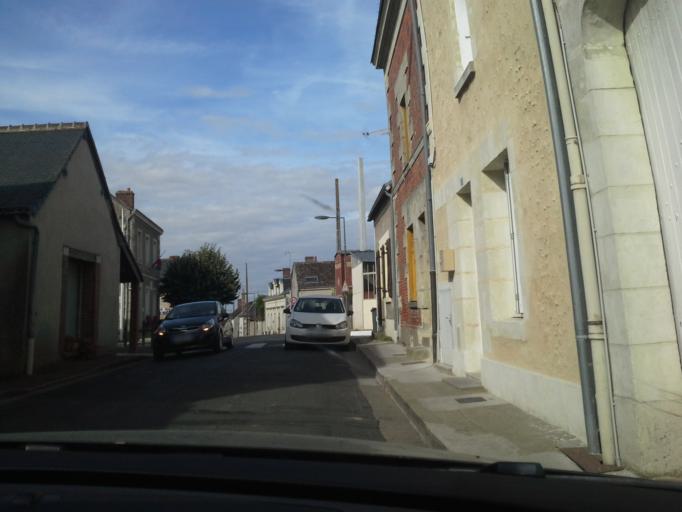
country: FR
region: Centre
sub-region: Departement d'Indre-et-Loire
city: Auzouer-en-Touraine
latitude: 47.5122
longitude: 0.9102
